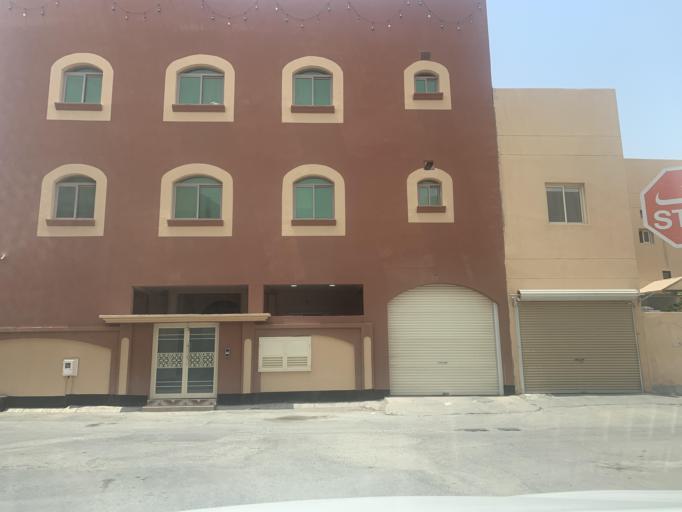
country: BH
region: Manama
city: Jidd Hafs
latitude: 26.2205
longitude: 50.4620
